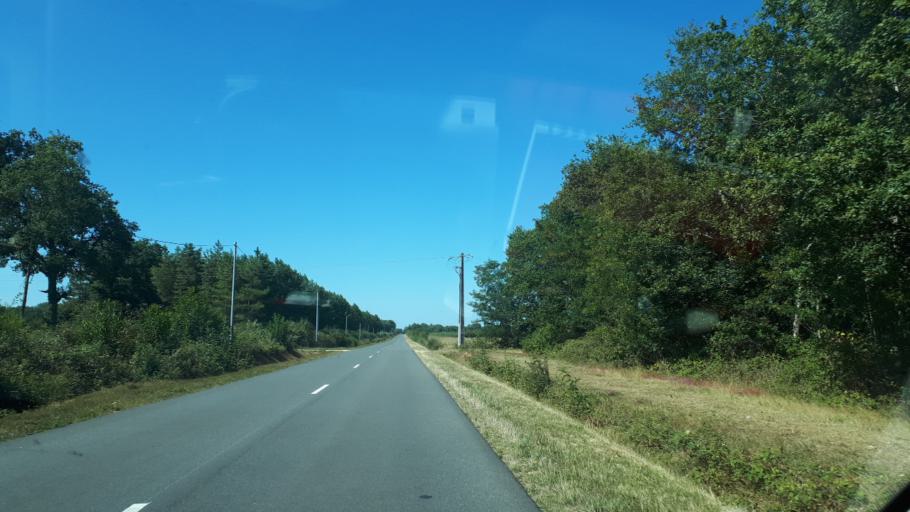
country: FR
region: Centre
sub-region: Departement du Cher
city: Brinon-sur-Sauldre
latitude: 47.6670
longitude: 2.2386
